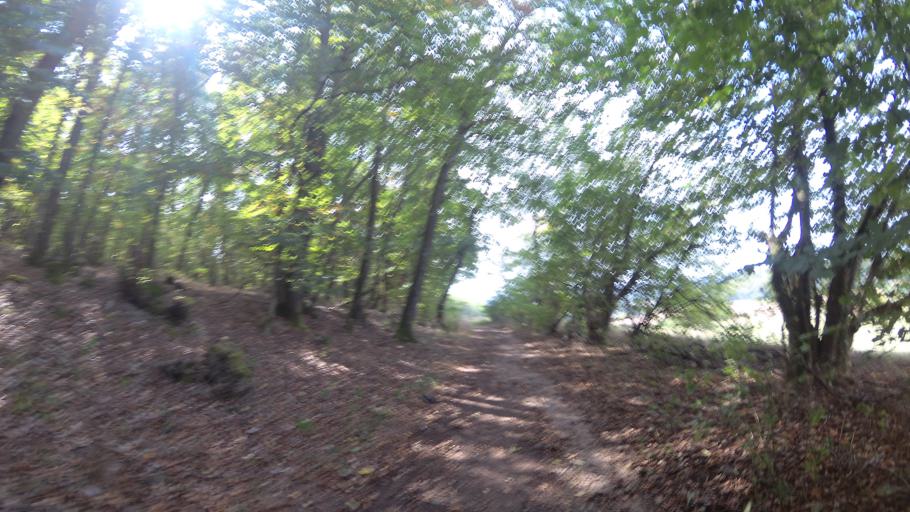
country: DE
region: Saarland
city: Sankt Wendel
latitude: 49.4832
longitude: 7.1907
